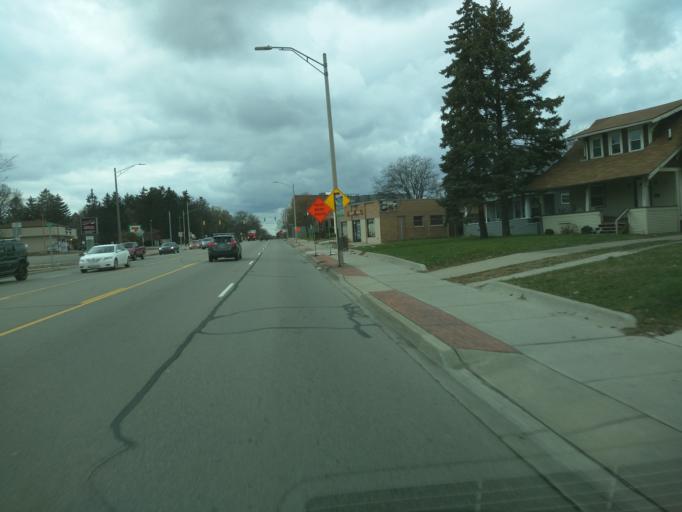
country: US
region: Michigan
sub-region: Ingham County
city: East Lansing
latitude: 42.7315
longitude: -84.4700
